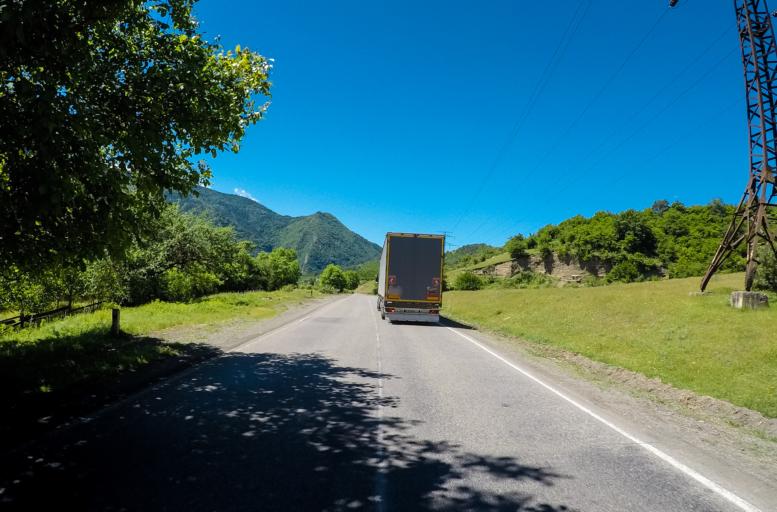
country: GE
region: Samtskhe-Javakheti
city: Borjomi
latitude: 41.7806
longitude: 43.2541
